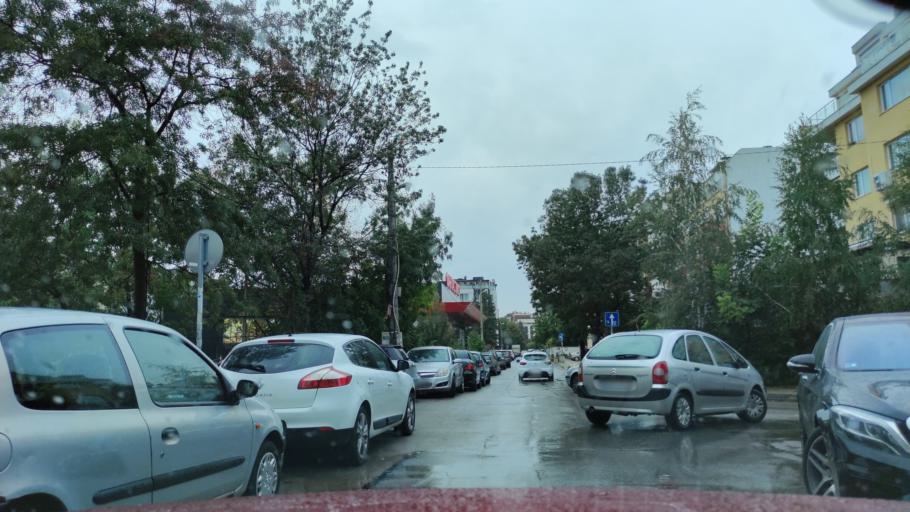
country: BG
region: Sofia-Capital
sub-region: Stolichna Obshtina
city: Sofia
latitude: 42.6653
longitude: 23.2813
